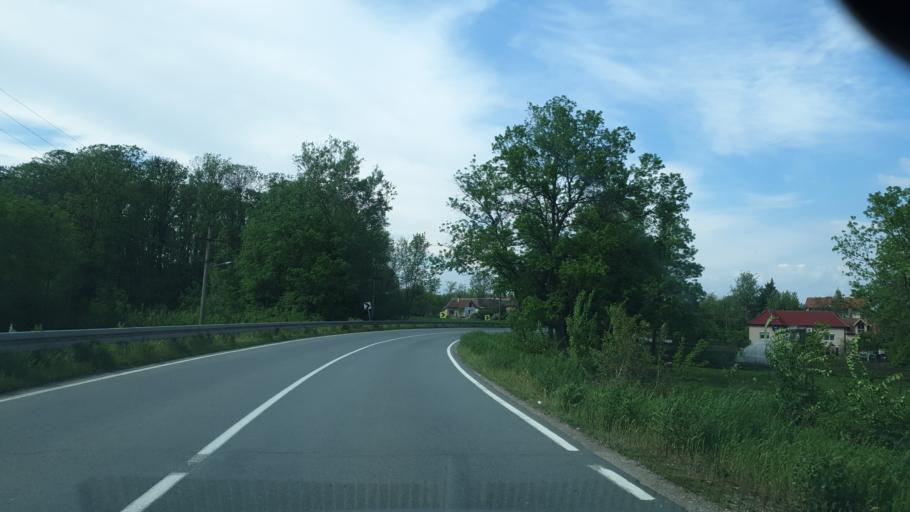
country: RS
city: Stubline
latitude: 44.5945
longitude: 20.1455
